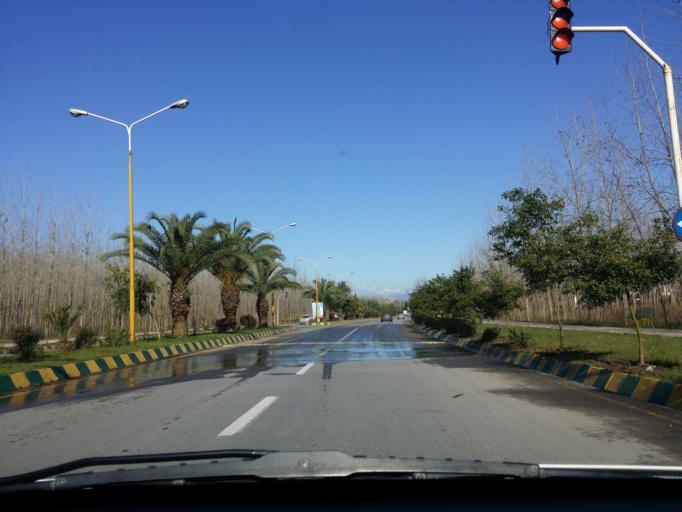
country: IR
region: Mazandaran
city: Chalus
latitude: 36.6726
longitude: 51.3067
